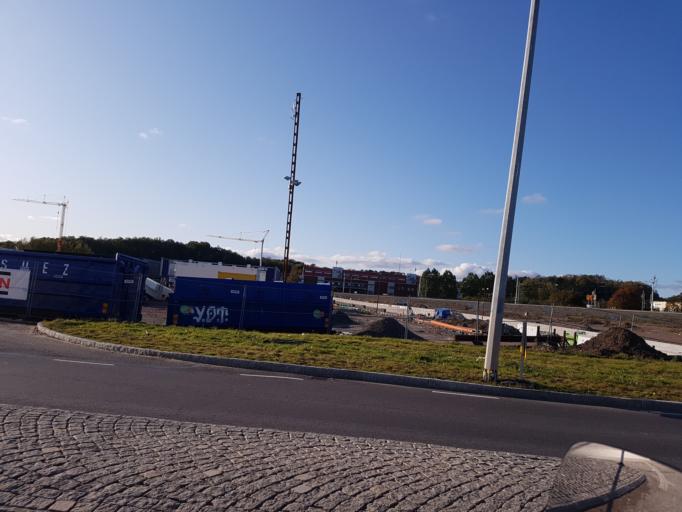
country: SE
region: Vaestra Goetaland
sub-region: Goteborg
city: Goeteborg
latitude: 57.7281
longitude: 11.9890
